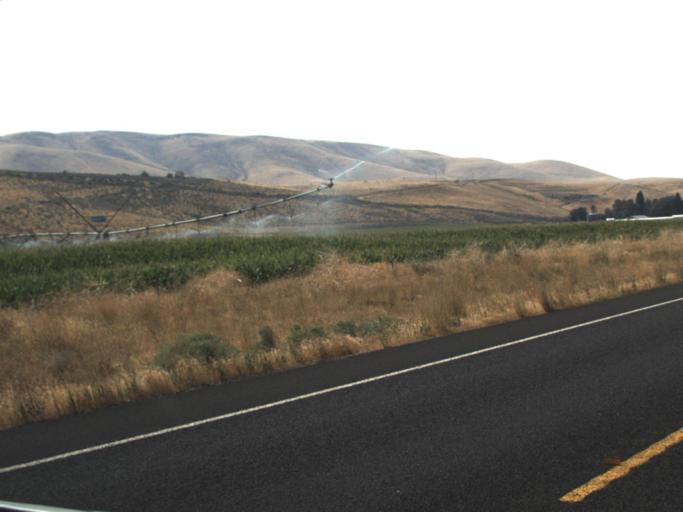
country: US
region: Washington
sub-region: Yakima County
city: Sunnyside
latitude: 46.5075
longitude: -120.0797
